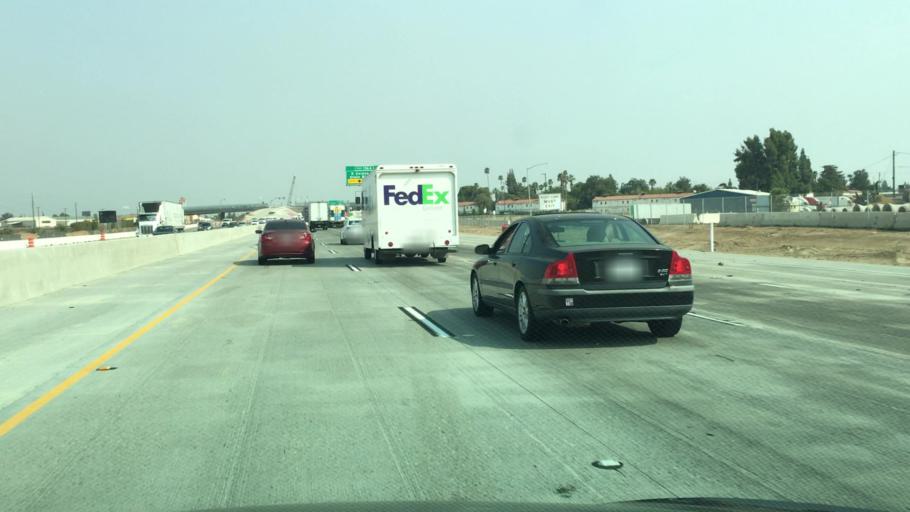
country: US
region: California
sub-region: Fresno County
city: West Park
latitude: 36.7767
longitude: -119.8434
